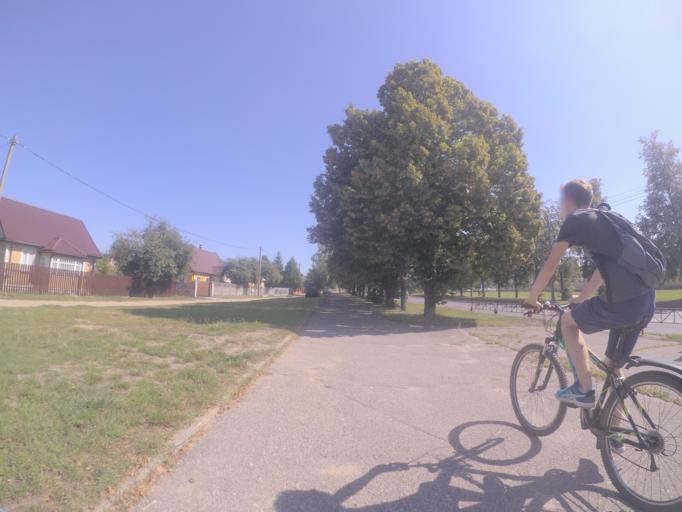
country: BY
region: Grodnenskaya
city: Hrodna
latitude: 53.6640
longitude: 23.7935
